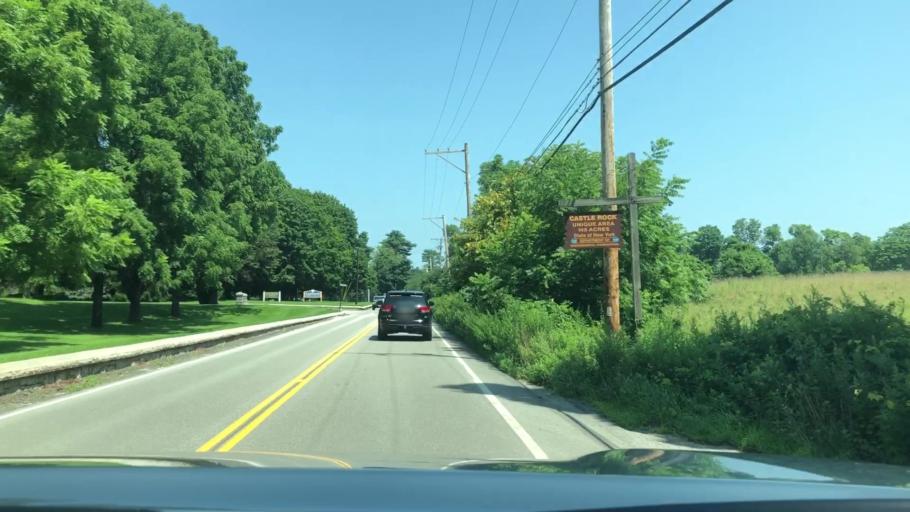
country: US
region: New York
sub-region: Orange County
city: Highland Falls
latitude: 41.3692
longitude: -73.9477
